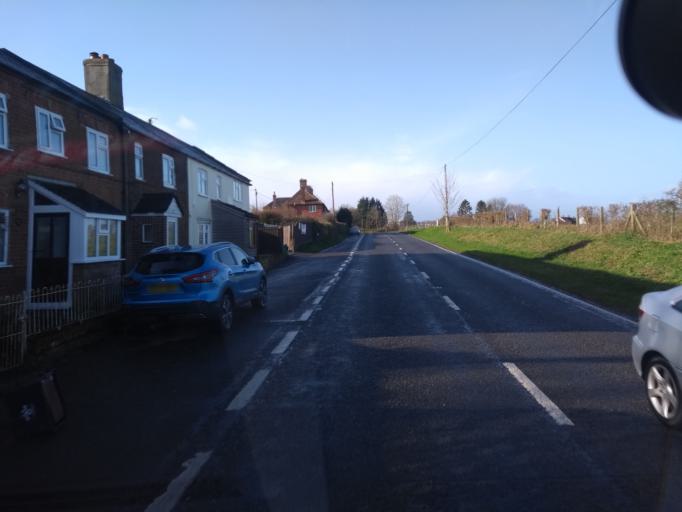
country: GB
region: England
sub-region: Somerset
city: Yeovil
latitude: 50.9700
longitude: -2.6129
